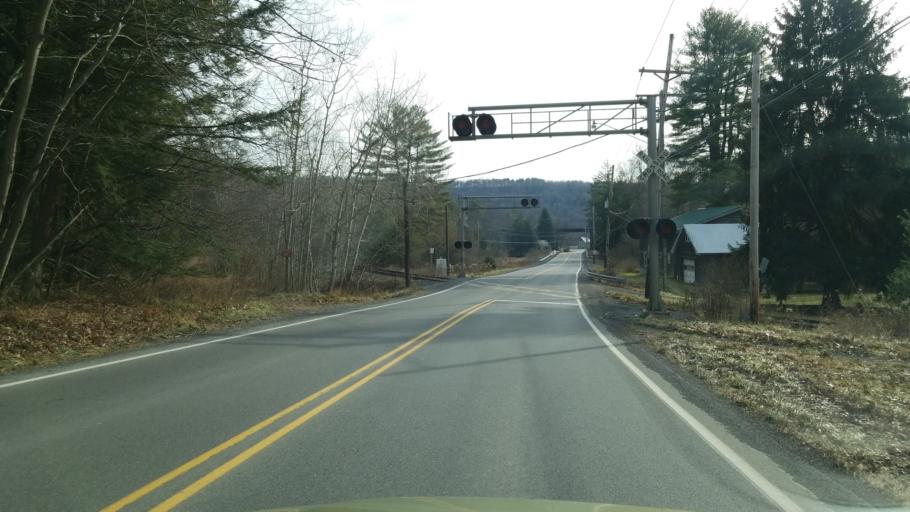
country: US
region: Pennsylvania
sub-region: Indiana County
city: Johnsonburg
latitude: 40.8853
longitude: -78.7672
